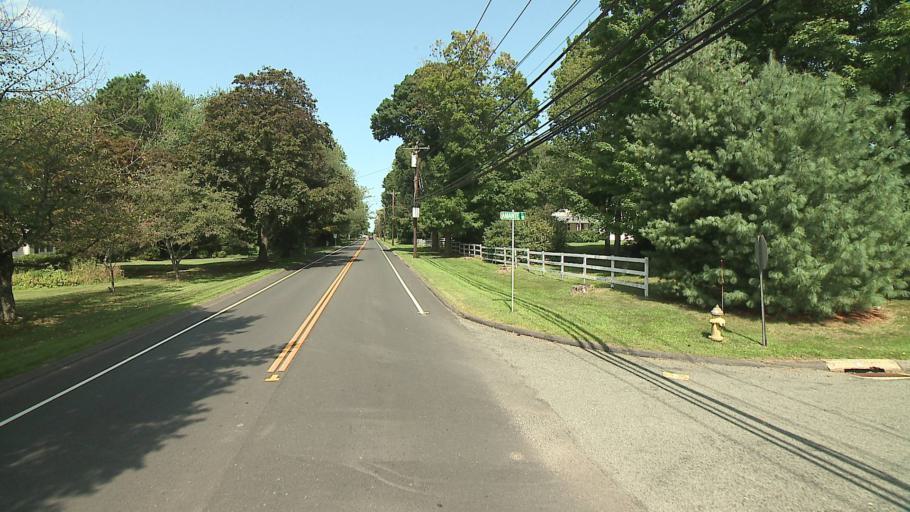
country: US
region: Connecticut
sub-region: Fairfield County
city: Trumbull
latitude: 41.2350
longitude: -73.2664
